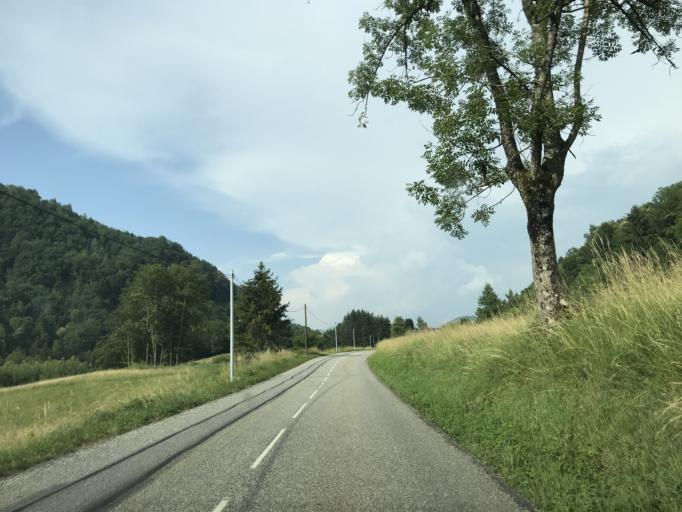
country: FR
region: Rhone-Alpes
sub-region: Departement de la Savoie
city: La Rochette
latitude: 45.4308
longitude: 6.1019
